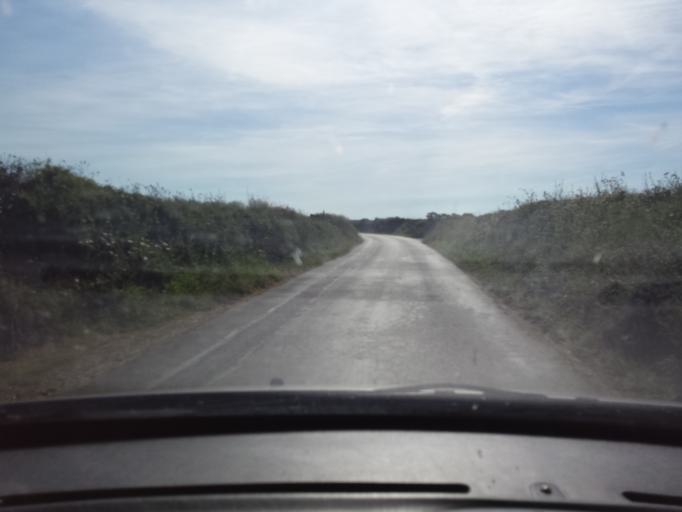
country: FR
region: Lower Normandy
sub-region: Departement de la Manche
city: Beaumont-Hague
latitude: 49.6758
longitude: -1.9290
